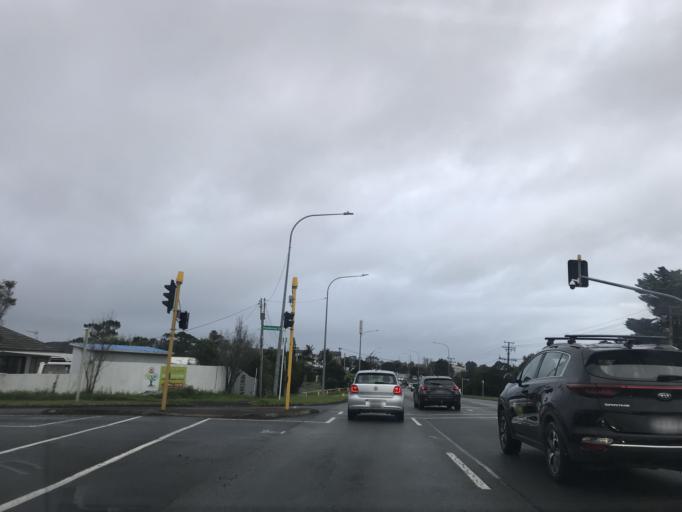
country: NZ
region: Auckland
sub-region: Auckland
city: Rothesay Bay
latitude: -36.7202
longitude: 174.7241
